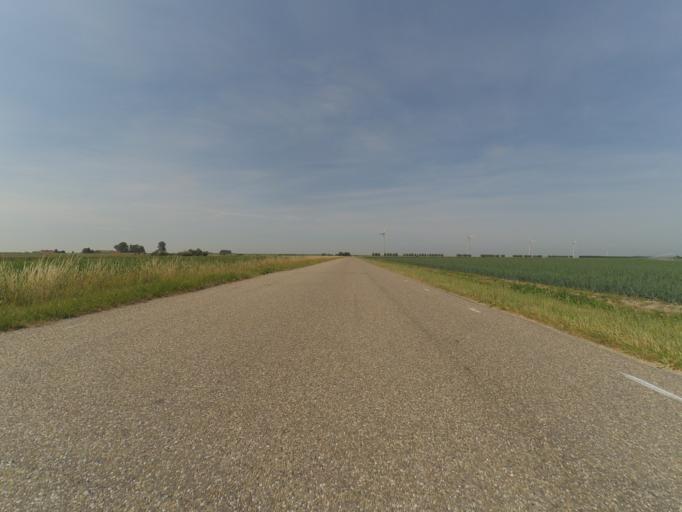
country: NL
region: Zeeland
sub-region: Schouwen-Duiveland
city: Bruinisse
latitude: 51.6344
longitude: 4.1362
